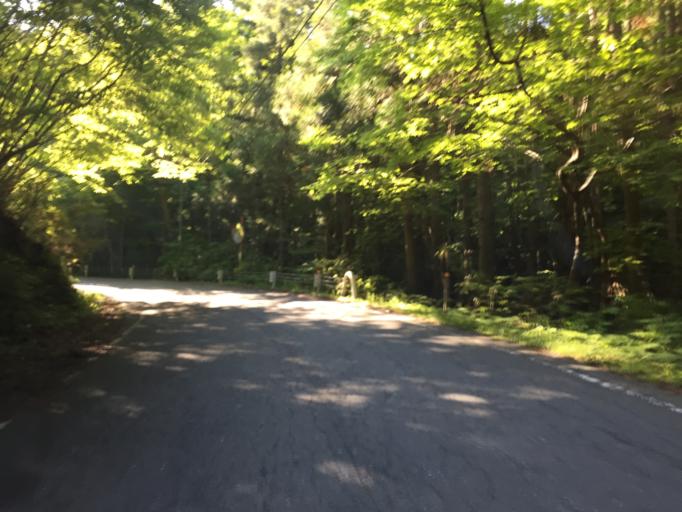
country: JP
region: Ibaraki
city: Kitaibaraki
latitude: 36.8852
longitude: 140.6285
